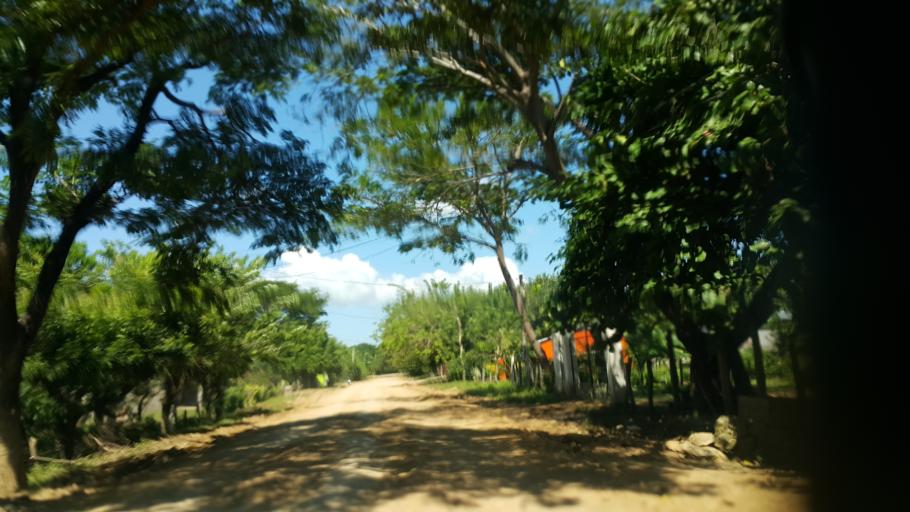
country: NI
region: Rivas
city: San Juan del Sur
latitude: 11.2863
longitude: -85.8898
